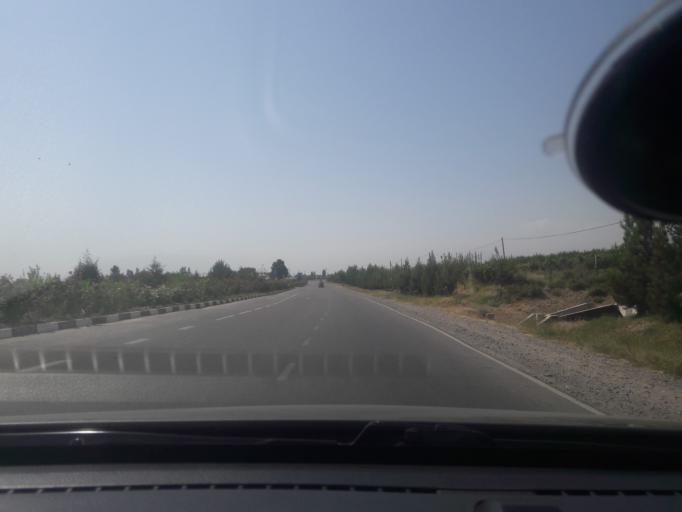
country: TJ
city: Shahrinav
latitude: 38.5615
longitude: 68.4335
